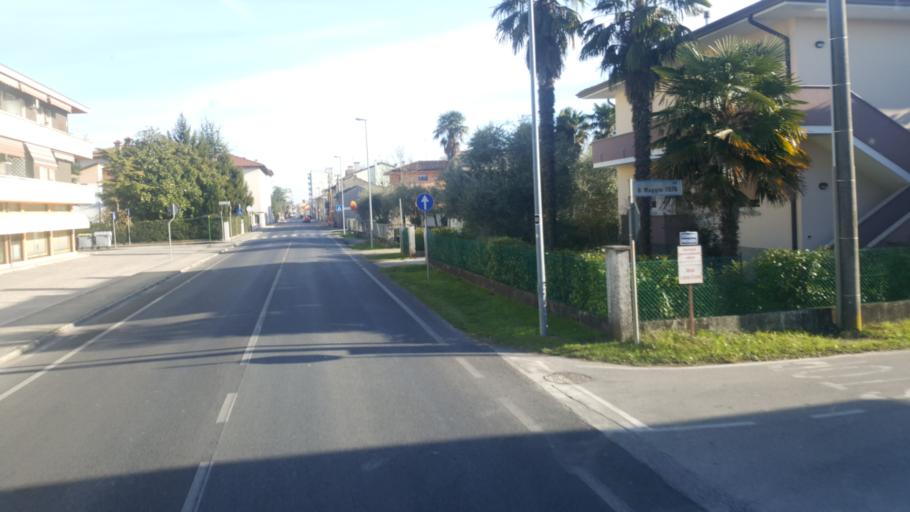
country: IT
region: Friuli Venezia Giulia
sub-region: Provincia di Udine
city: San Giorgio di Nogaro
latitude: 45.8335
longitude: 13.2011
